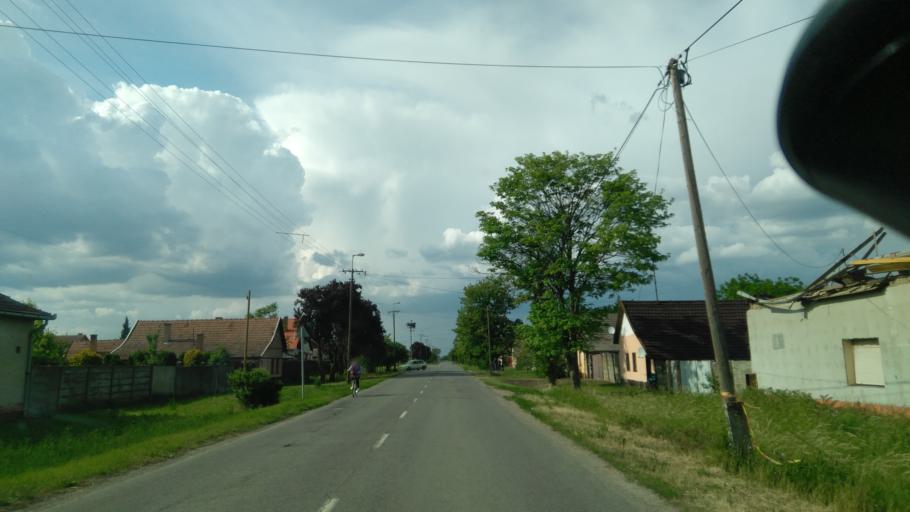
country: HU
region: Bekes
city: Battonya
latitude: 46.2881
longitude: 21.0348
